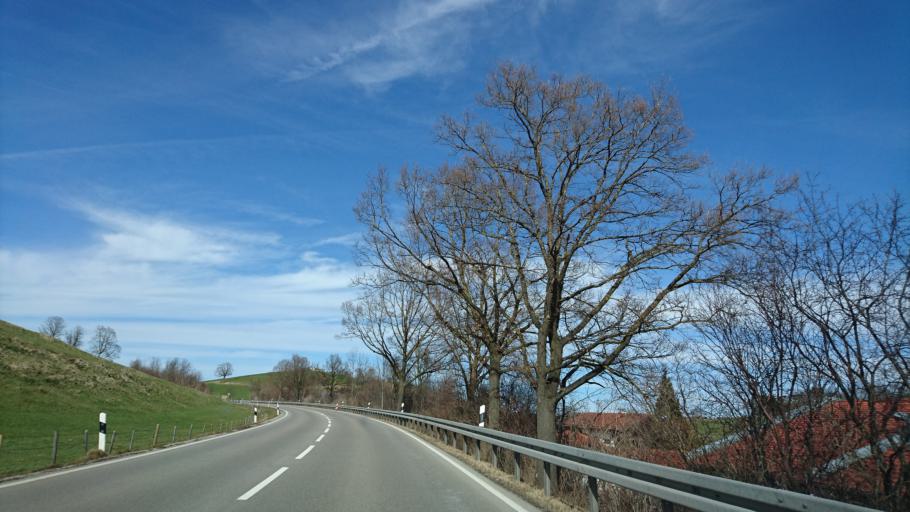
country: DE
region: Bavaria
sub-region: Swabia
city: Rosshaupten
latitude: 47.6111
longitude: 10.7141
